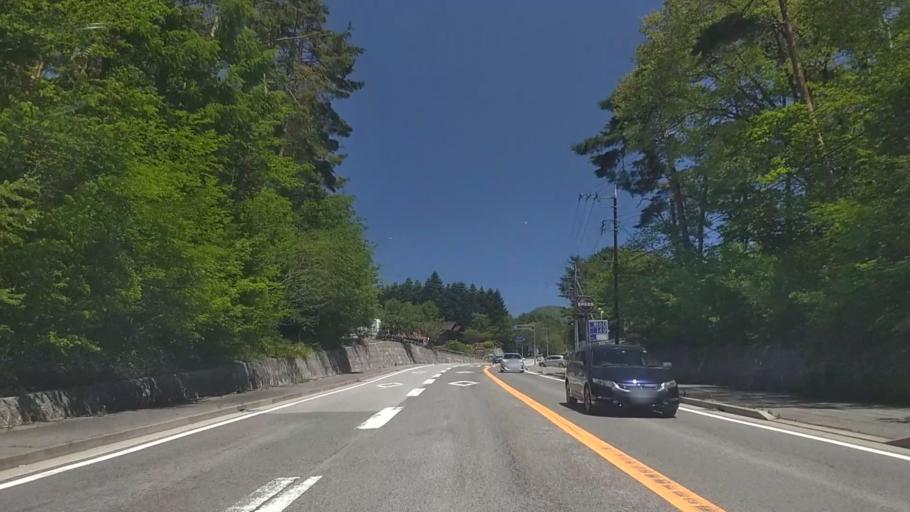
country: JP
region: Yamanashi
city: Nirasaki
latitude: 35.8998
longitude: 138.4420
